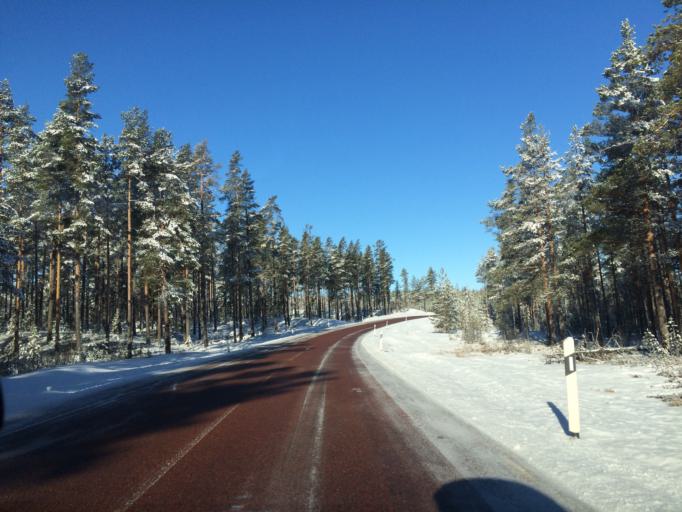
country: SE
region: Dalarna
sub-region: Mora Kommun
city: Mora
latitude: 60.8483
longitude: 14.2641
